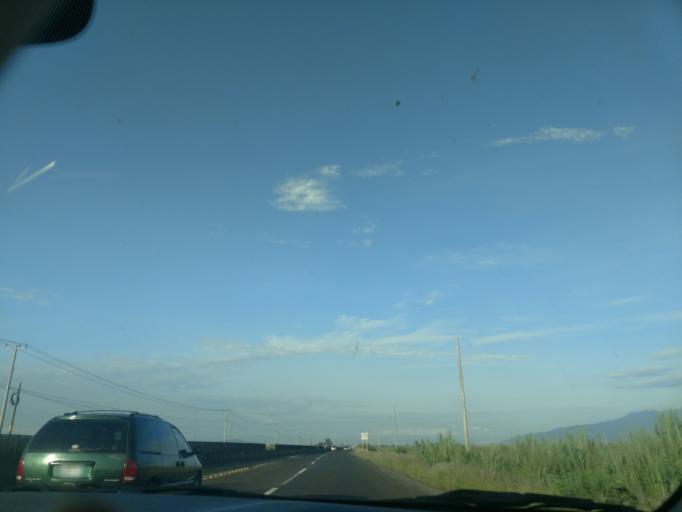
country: MX
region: Jalisco
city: El Refugio
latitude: 20.6432
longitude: -103.7565
